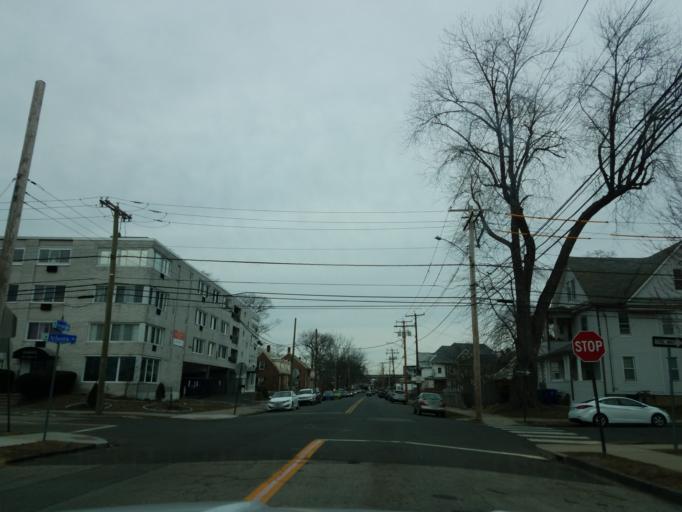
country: US
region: Connecticut
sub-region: Fairfield County
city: Bridgeport
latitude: 41.1641
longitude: -73.1965
